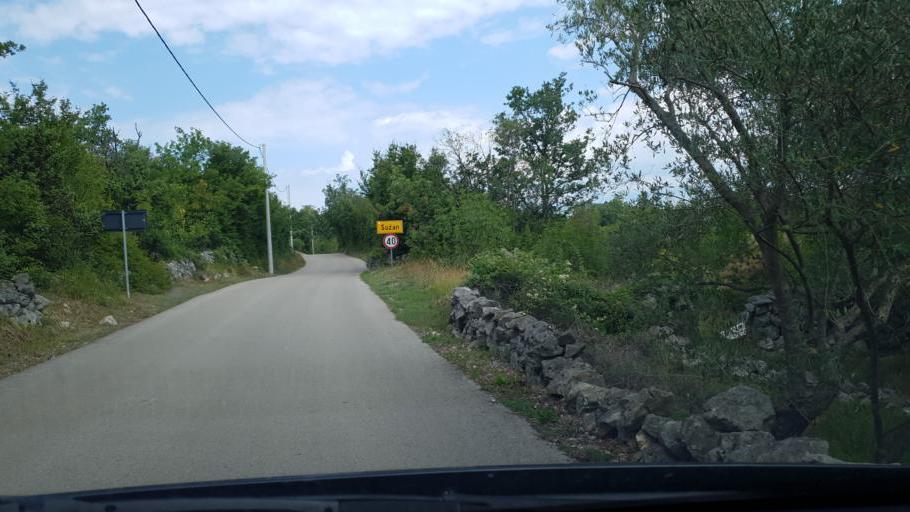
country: HR
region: Primorsko-Goranska
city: Njivice
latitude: 45.1459
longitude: 14.5802
